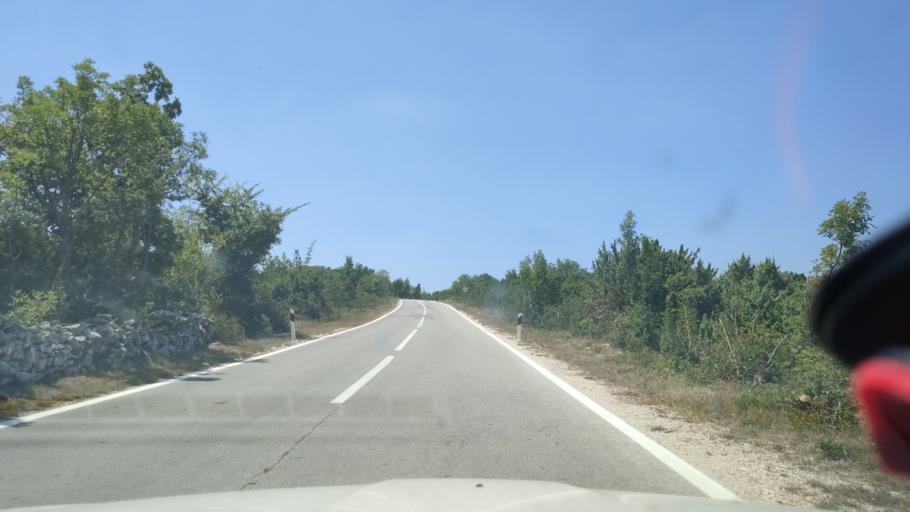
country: HR
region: Sibensko-Kniniska
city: Kistanje
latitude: 44.0070
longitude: 16.0027
